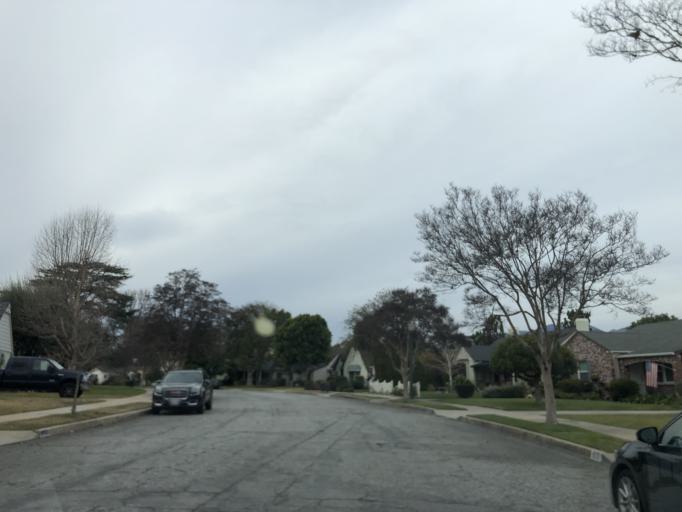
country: US
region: California
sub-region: Los Angeles County
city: San Gabriel
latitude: 34.1064
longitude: -118.1090
